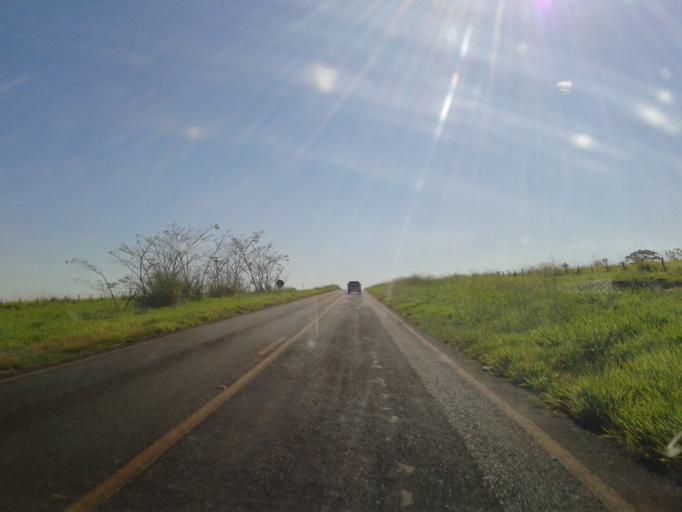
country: BR
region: Minas Gerais
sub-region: Capinopolis
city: Capinopolis
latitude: -18.6232
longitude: -49.5351
